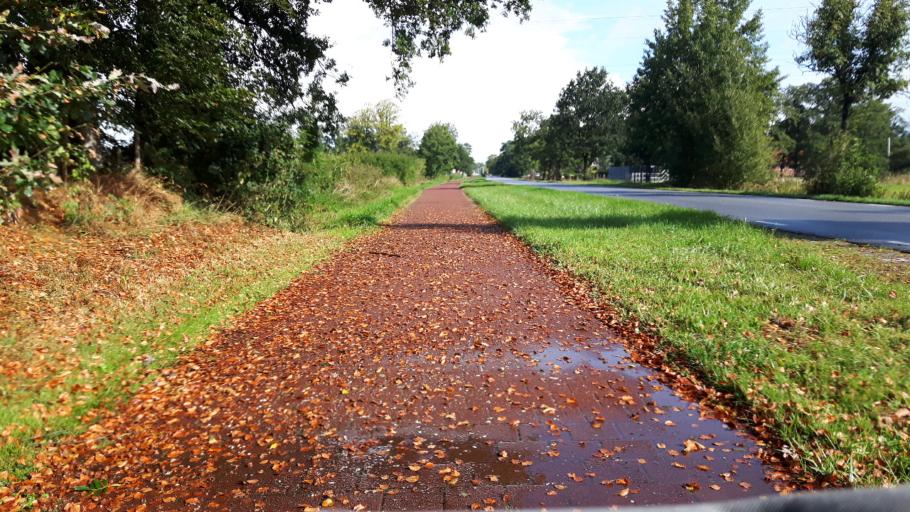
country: NL
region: Friesland
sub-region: Gemeente Smallingerland
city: Drachten
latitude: 53.0824
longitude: 6.0999
